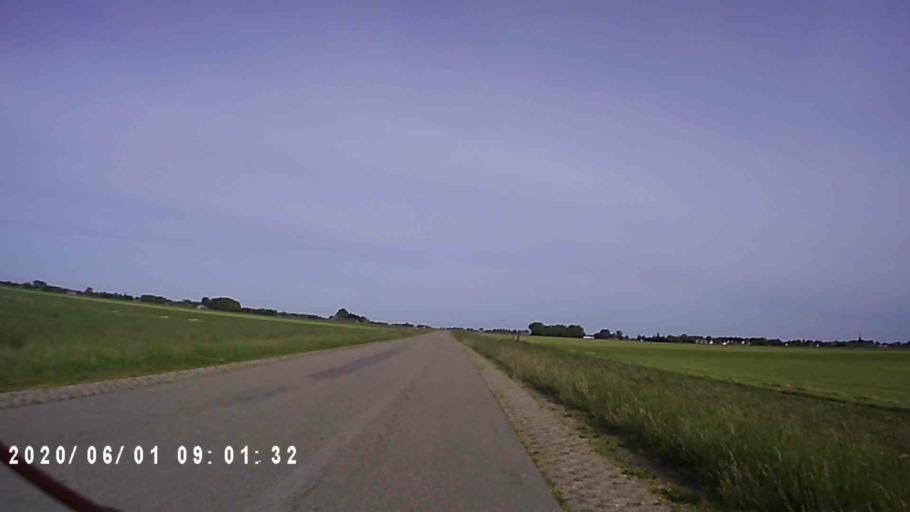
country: NL
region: Friesland
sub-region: Gemeente Ferwerderadiel
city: Hallum
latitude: 53.2916
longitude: 5.7879
